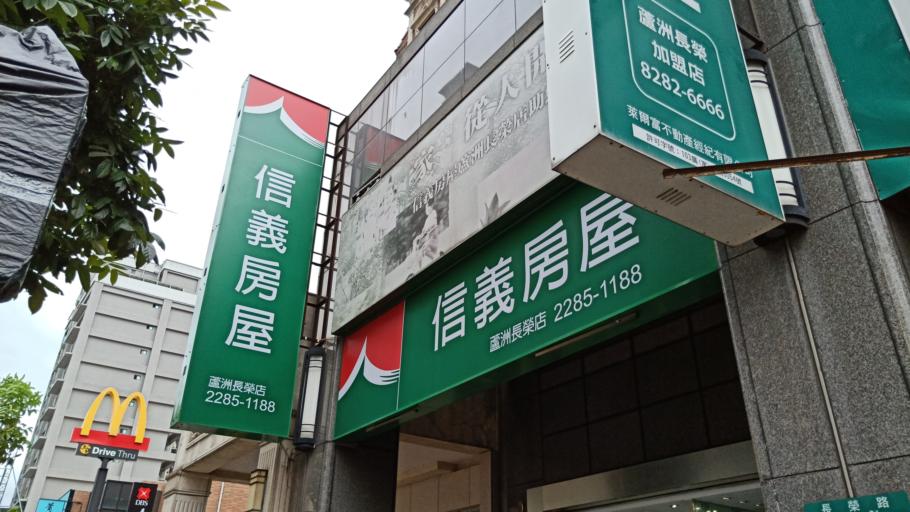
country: TW
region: Taipei
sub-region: Taipei
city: Banqiao
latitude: 25.0868
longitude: 121.4600
